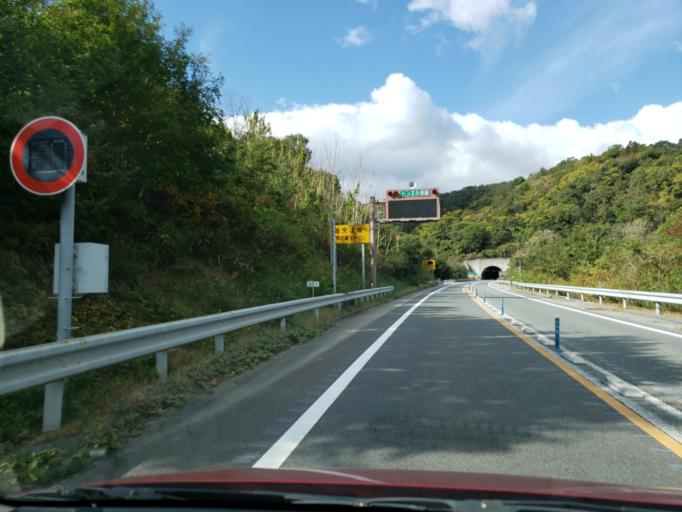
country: JP
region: Tokushima
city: Kamojimacho-jogejima
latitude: 34.1046
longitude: 134.2968
